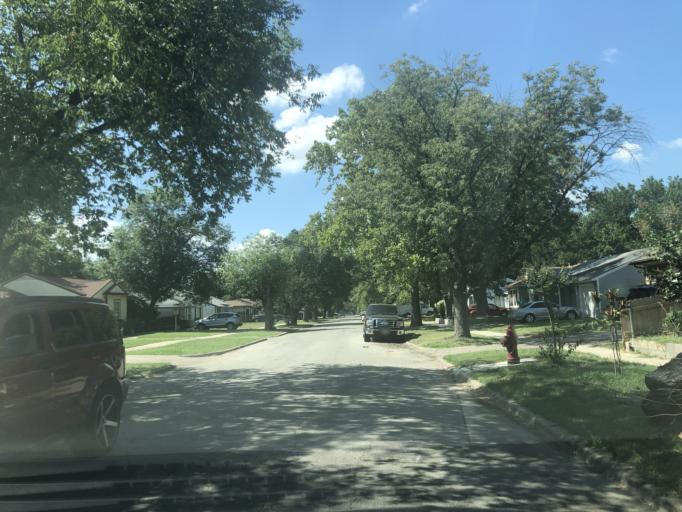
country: US
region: Texas
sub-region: Dallas County
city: Grand Prairie
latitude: 32.7345
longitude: -97.0101
